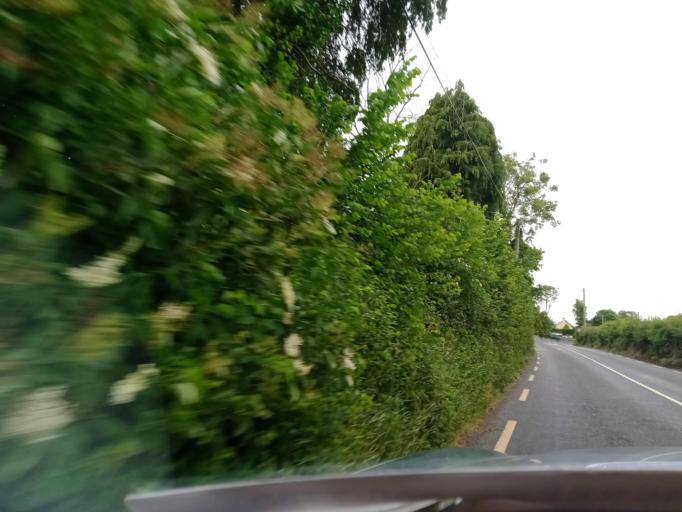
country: IE
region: Leinster
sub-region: Kilkenny
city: Piltown
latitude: 52.4688
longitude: -7.2661
